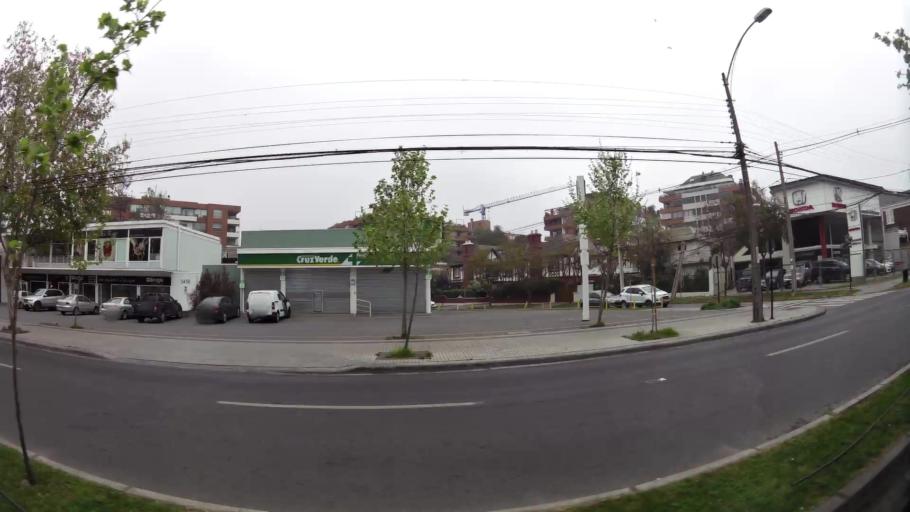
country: CL
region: Santiago Metropolitan
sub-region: Provincia de Santiago
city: Villa Presidente Frei, Nunoa, Santiago, Chile
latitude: -33.4043
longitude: -70.5966
